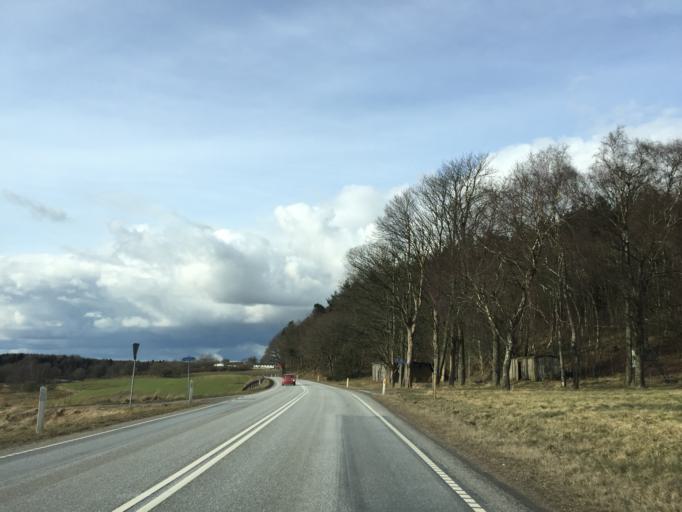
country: DK
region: Central Jutland
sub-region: Favrskov Kommune
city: Hammel
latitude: 56.2135
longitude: 9.7681
